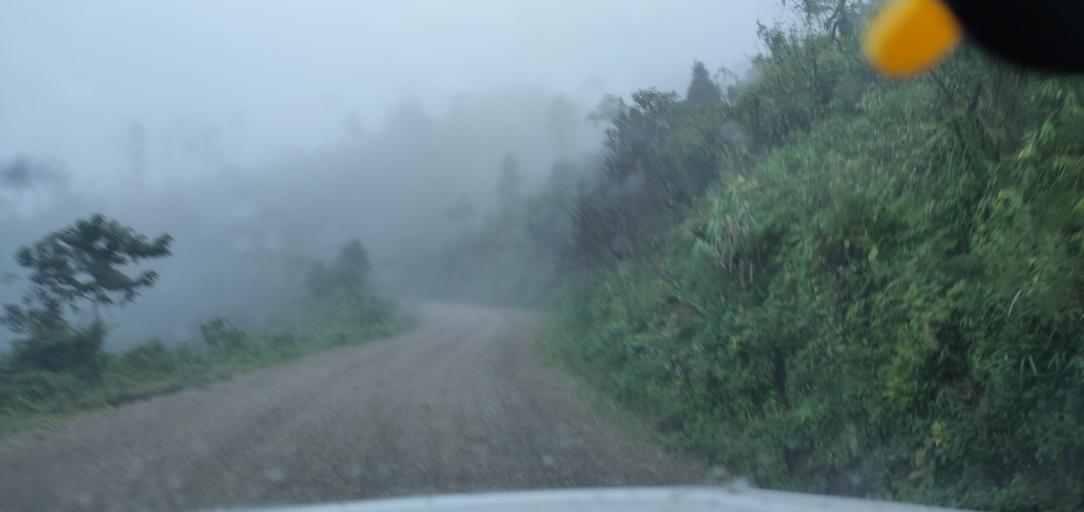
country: LA
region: Phongsali
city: Phongsali
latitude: 21.3976
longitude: 102.1924
